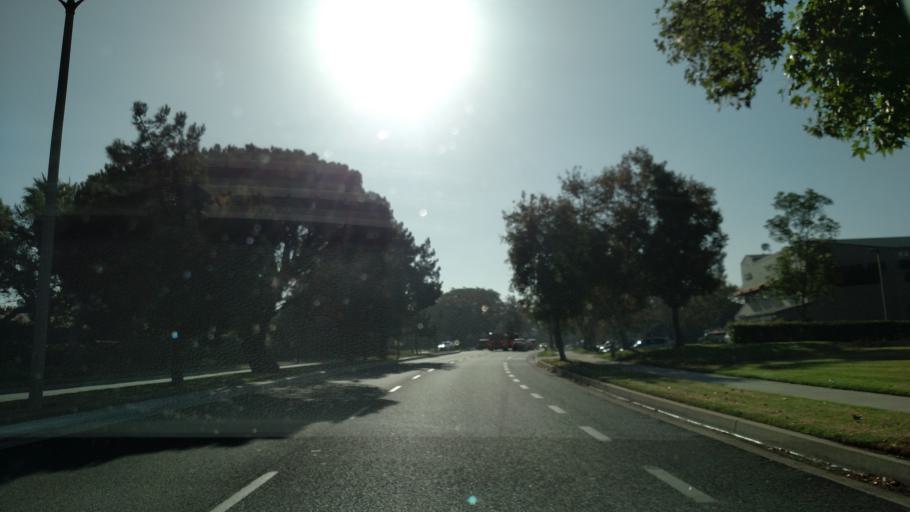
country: US
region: California
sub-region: Orange County
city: Irvine
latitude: 33.6805
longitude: -117.8022
